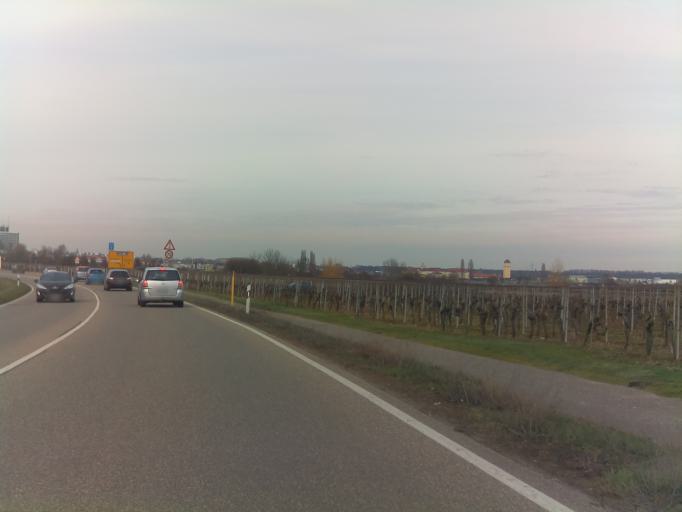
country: DE
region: Rheinland-Pfalz
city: Neustadt
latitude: 49.3268
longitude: 8.1512
